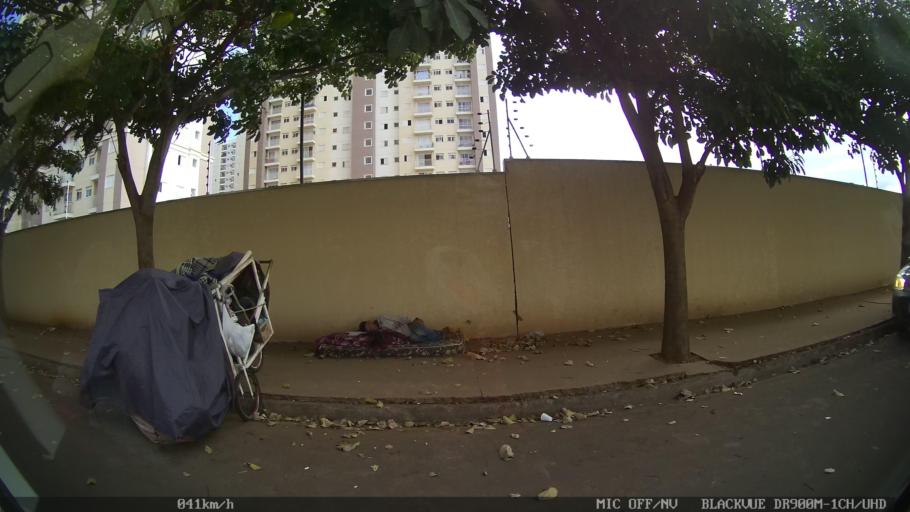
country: BR
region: Sao Paulo
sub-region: Americana
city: Americana
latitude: -22.7224
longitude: -47.3173
